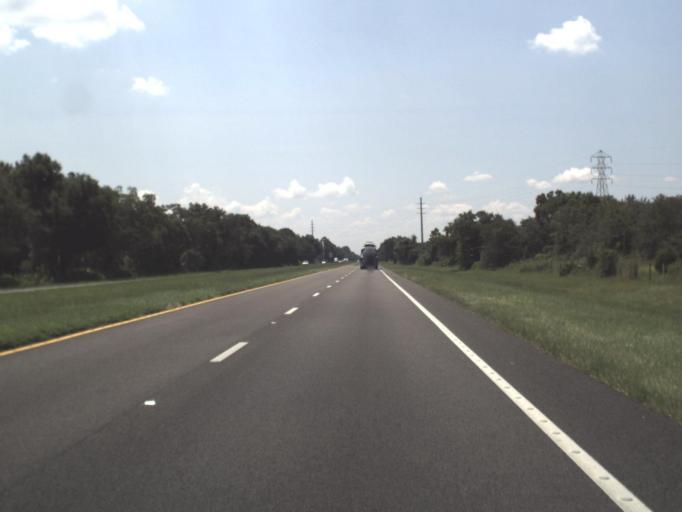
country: US
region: Florida
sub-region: Levy County
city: Inglis
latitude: 28.9983
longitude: -82.6539
